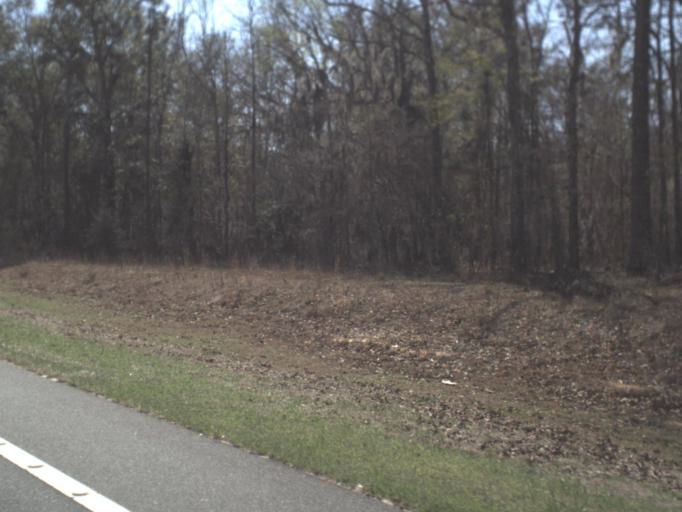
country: US
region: Florida
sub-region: Jackson County
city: Sneads
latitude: 30.6472
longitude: -85.0382
